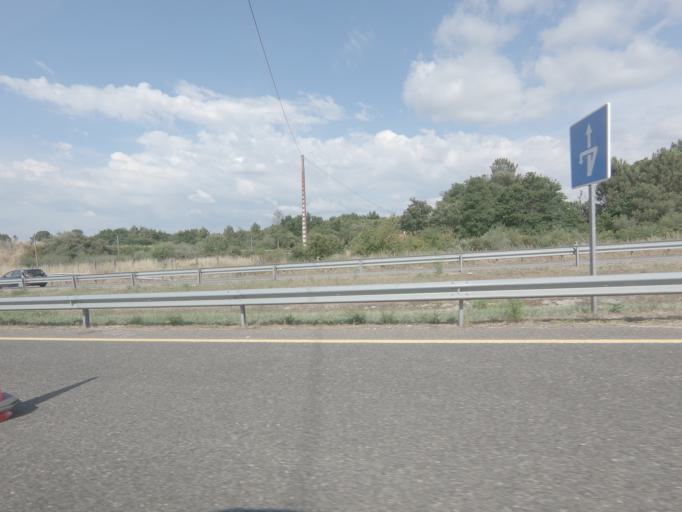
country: ES
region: Galicia
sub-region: Provincia de Ourense
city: Taboadela
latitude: 42.2556
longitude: -7.8690
